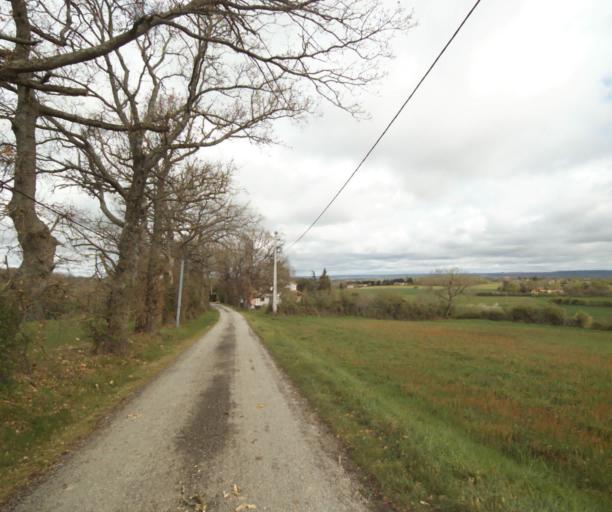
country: FR
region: Midi-Pyrenees
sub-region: Departement de l'Ariege
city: Saverdun
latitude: 43.2177
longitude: 1.5618
